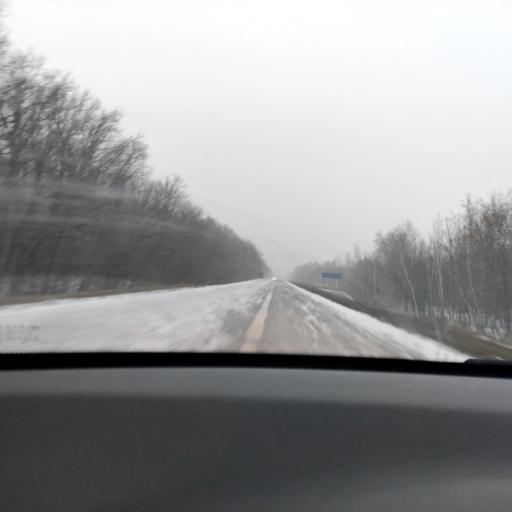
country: RU
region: Samara
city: Novokuybyshevsk
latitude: 52.9605
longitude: 49.8907
